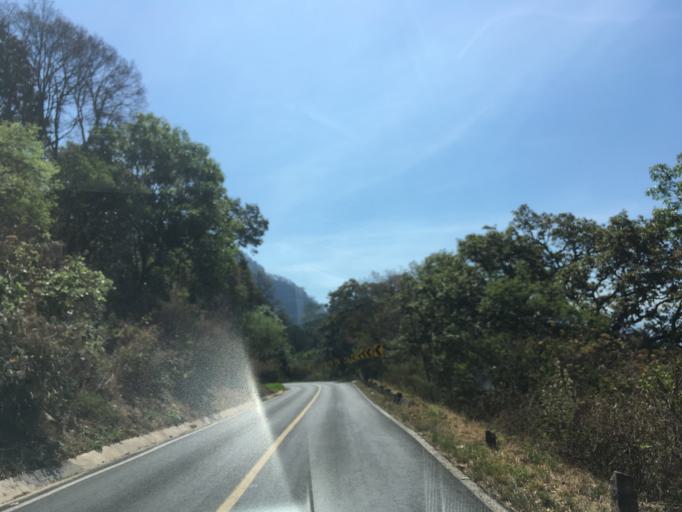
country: MX
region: Michoacan
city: Tzitzio
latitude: 19.6491
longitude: -100.9613
